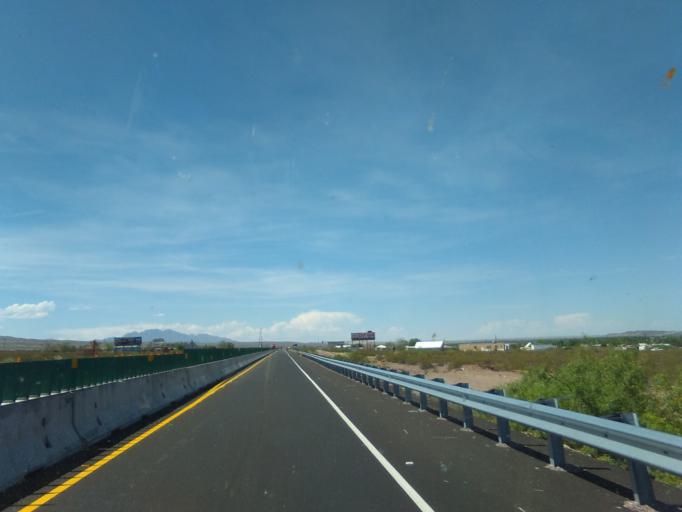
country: US
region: New Mexico
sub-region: Socorro County
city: Socorro
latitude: 34.1495
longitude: -106.9150
